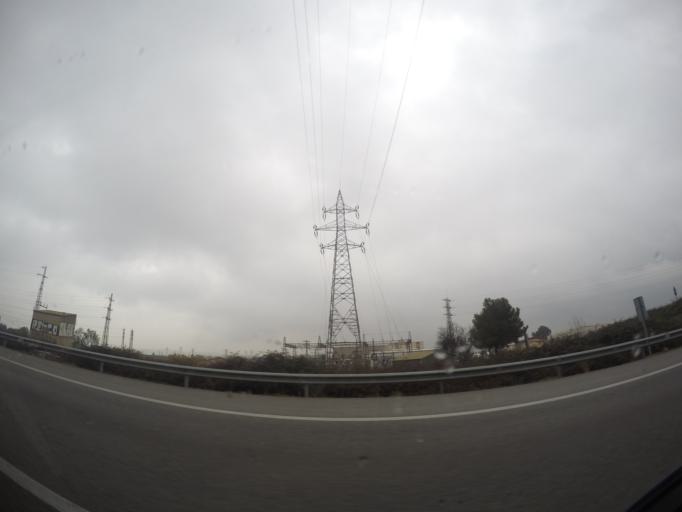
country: ES
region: Catalonia
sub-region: Provincia de Barcelona
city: Vilafranca del Penedes
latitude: 41.3294
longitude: 1.7035
